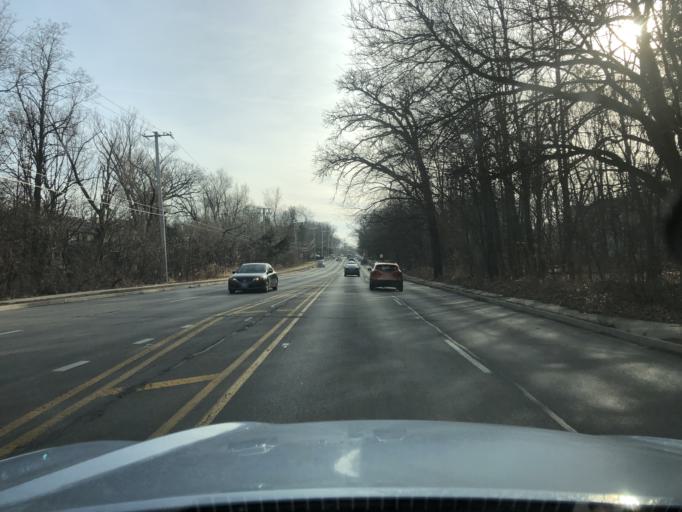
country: US
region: Illinois
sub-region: DuPage County
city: Roselle
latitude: 41.9731
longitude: -88.0803
